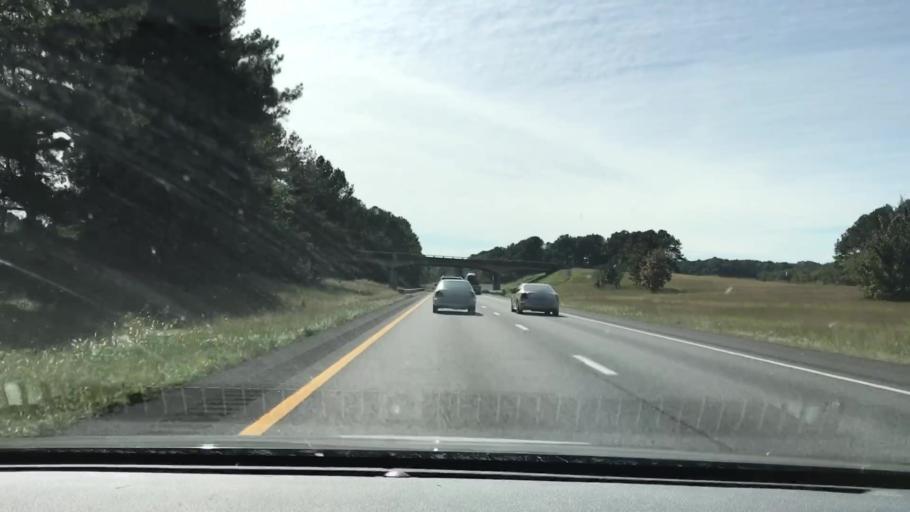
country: US
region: Tennessee
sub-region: Sumner County
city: Portland
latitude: 36.5924
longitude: -86.5994
